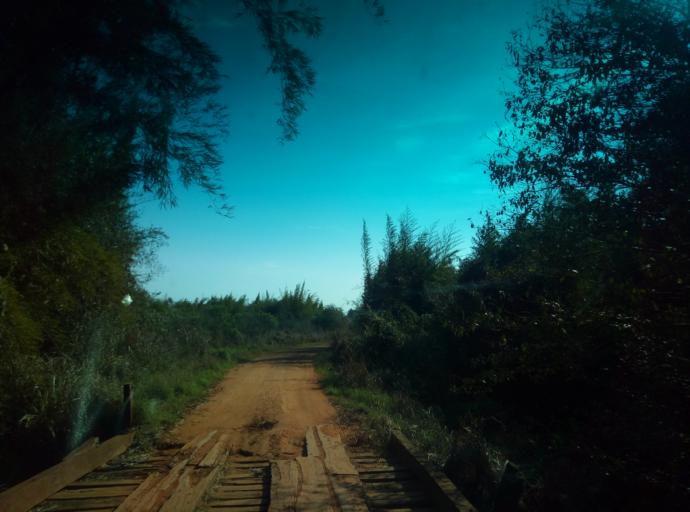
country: PY
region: Caaguazu
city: Doctor Cecilio Baez
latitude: -25.1648
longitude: -56.2225
